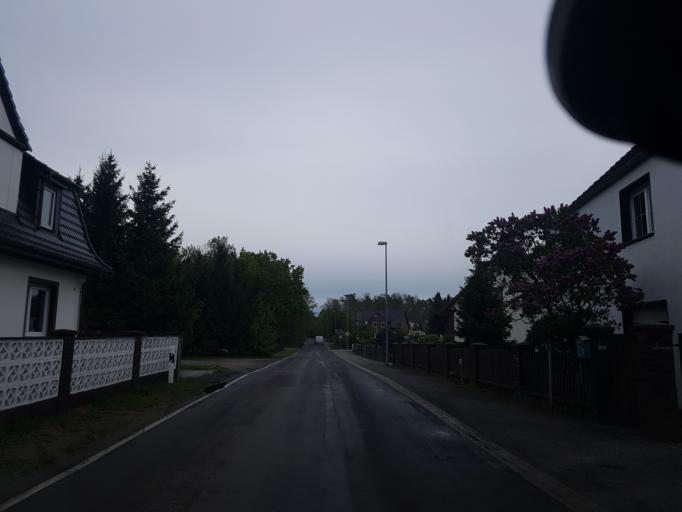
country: DE
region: Brandenburg
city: Spremberg
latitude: 51.6083
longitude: 14.4013
